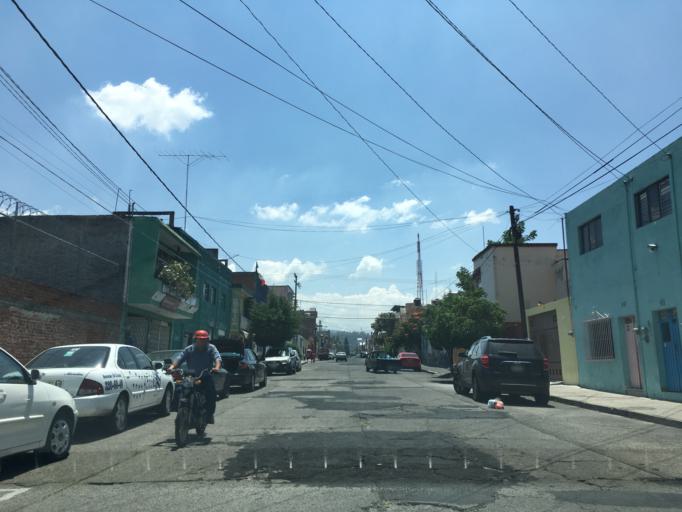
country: MX
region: Michoacan
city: Morelia
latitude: 19.7019
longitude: -101.1710
